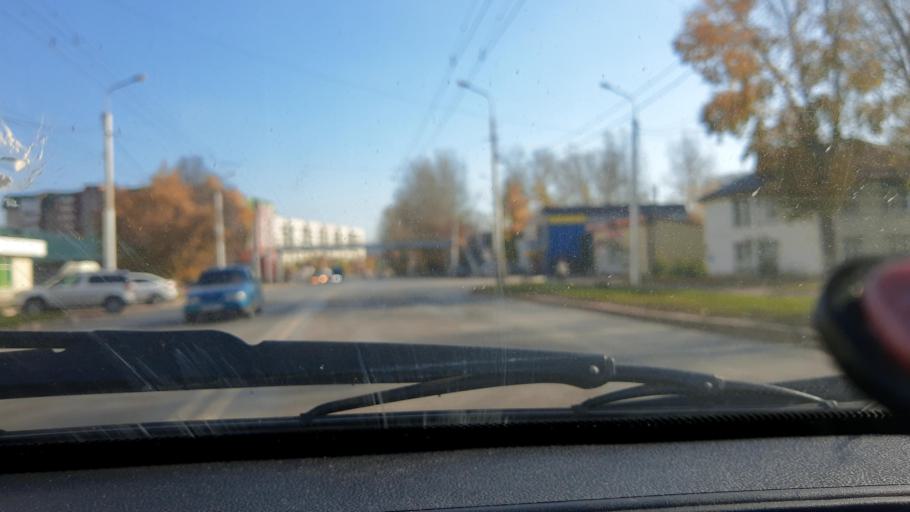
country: RU
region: Bashkortostan
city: Mikhaylovka
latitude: 54.7891
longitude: 55.8816
